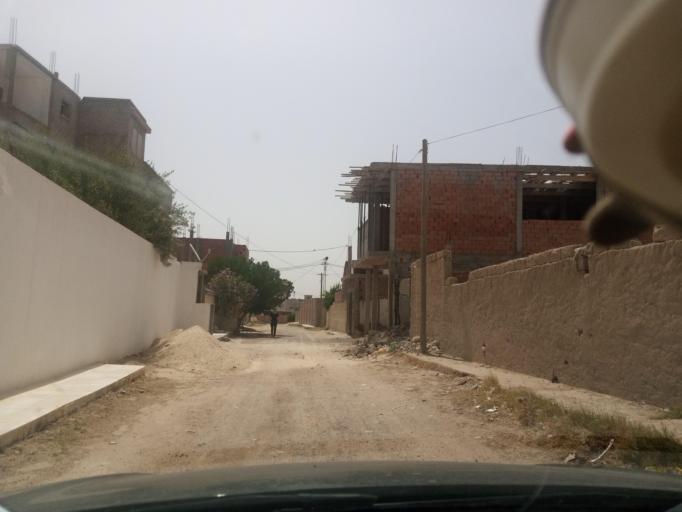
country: TN
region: Al Qasrayn
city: Kasserine
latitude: 35.2132
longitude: 8.8966
